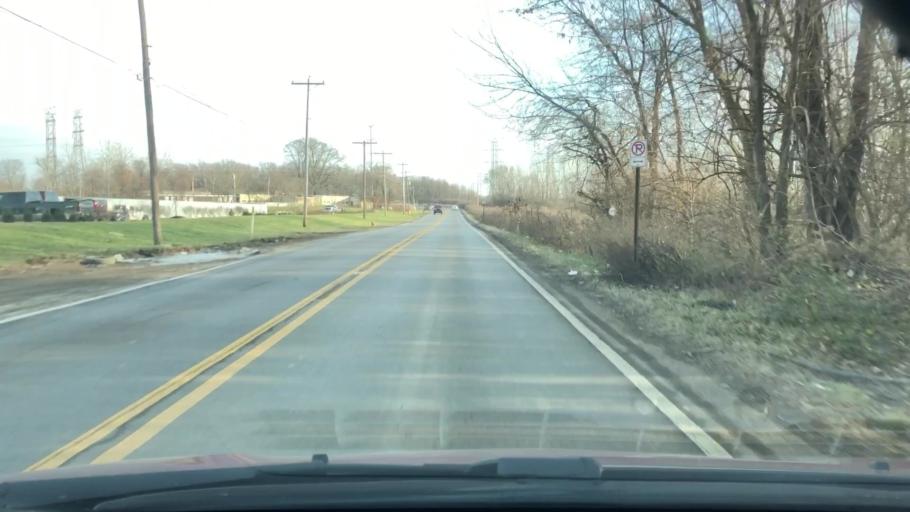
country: US
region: Ohio
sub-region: Franklin County
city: Obetz
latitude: 39.9087
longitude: -82.9739
